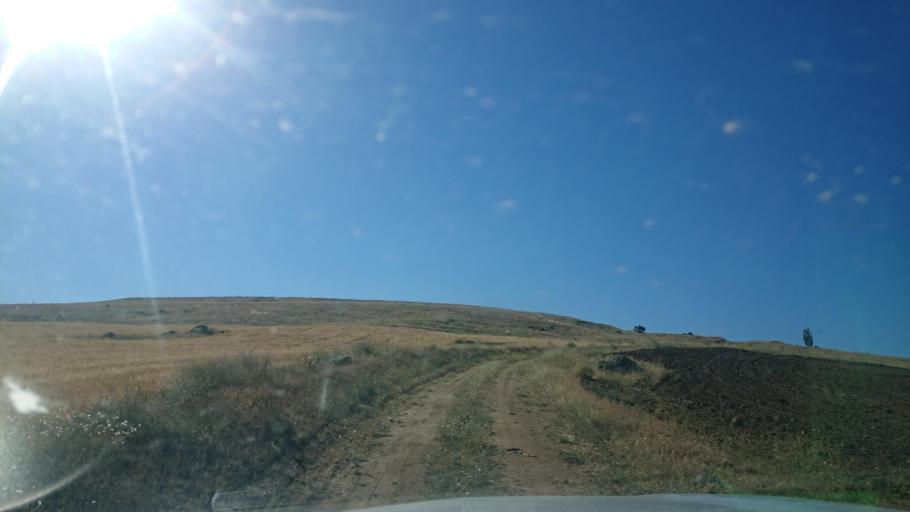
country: TR
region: Aksaray
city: Agacoren
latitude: 38.8387
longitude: 33.9355
